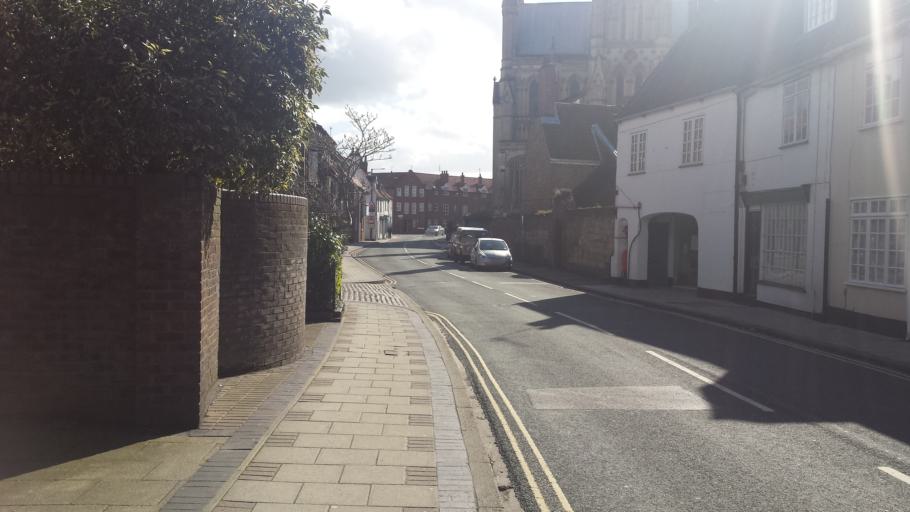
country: GB
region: England
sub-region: East Riding of Yorkshire
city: Beverley
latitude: 53.8404
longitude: -0.4247
